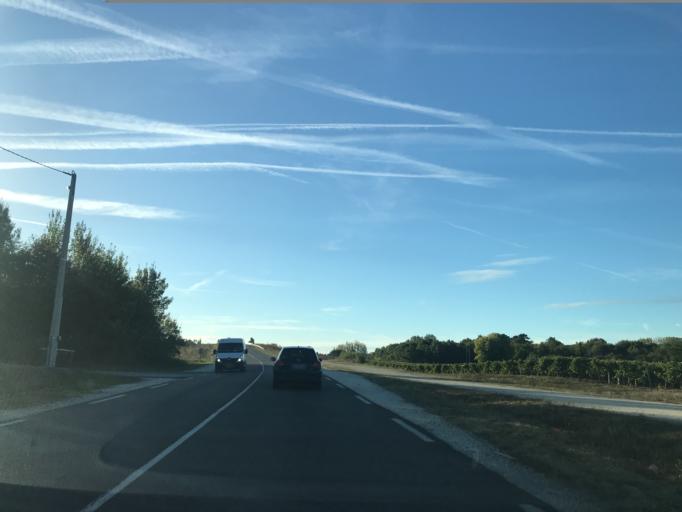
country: FR
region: Poitou-Charentes
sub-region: Departement de la Charente-Maritime
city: Montguyon
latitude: 45.2086
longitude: -0.1640
